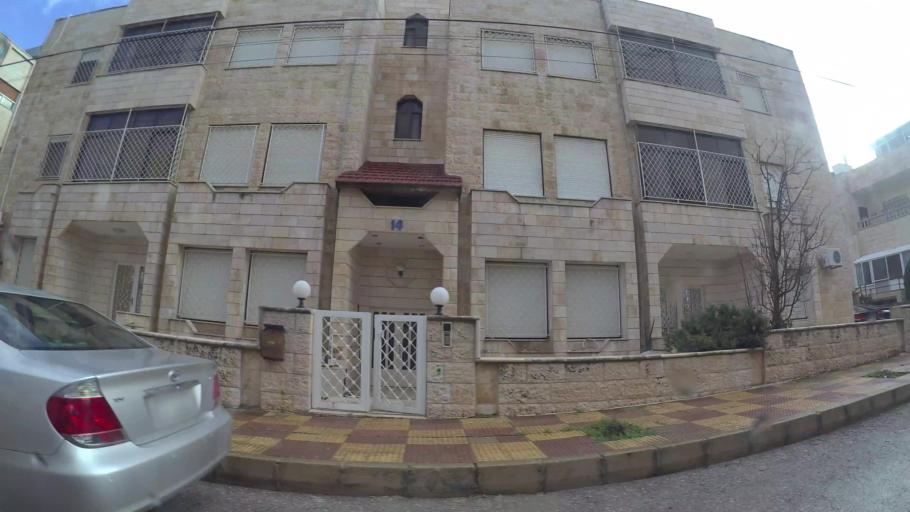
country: JO
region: Amman
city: Al Jubayhah
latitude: 32.0300
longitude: 35.8656
